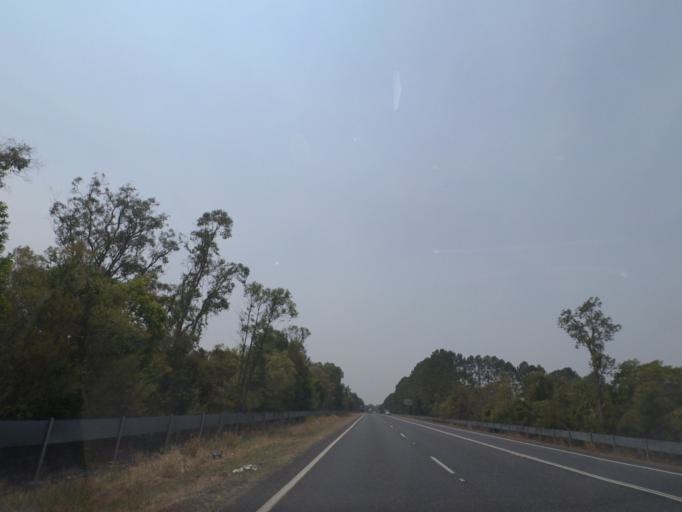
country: AU
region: New South Wales
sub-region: Ballina
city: Ballina
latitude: -28.9424
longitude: 153.4688
